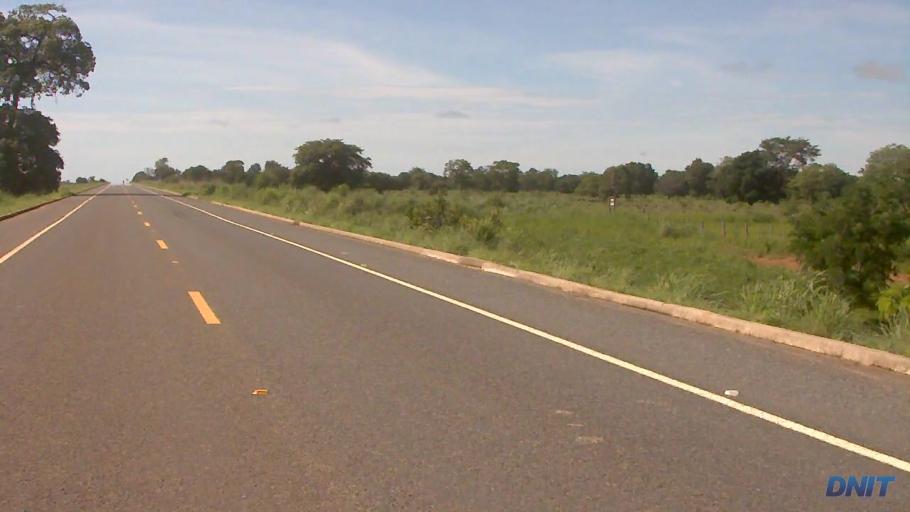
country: BR
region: Goias
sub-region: Sao Miguel Do Araguaia
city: Sao Miguel do Araguaia
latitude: -13.4271
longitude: -50.1274
